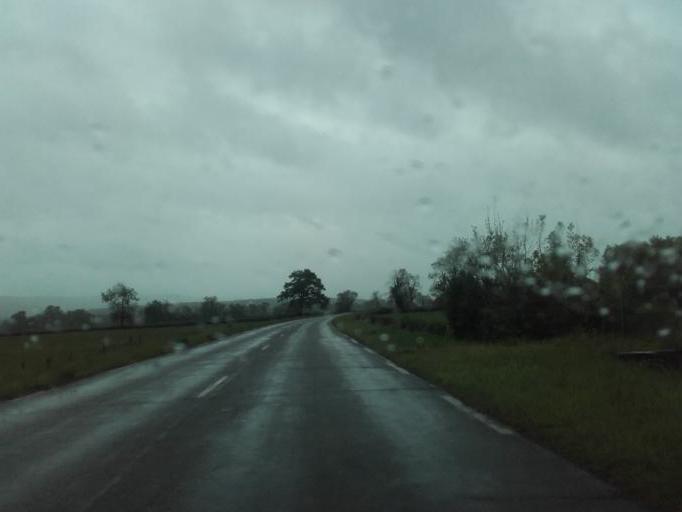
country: FR
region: Bourgogne
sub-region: Departement de Saone-et-Loire
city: Saint-Gengoux-le-National
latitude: 46.5279
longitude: 4.6863
